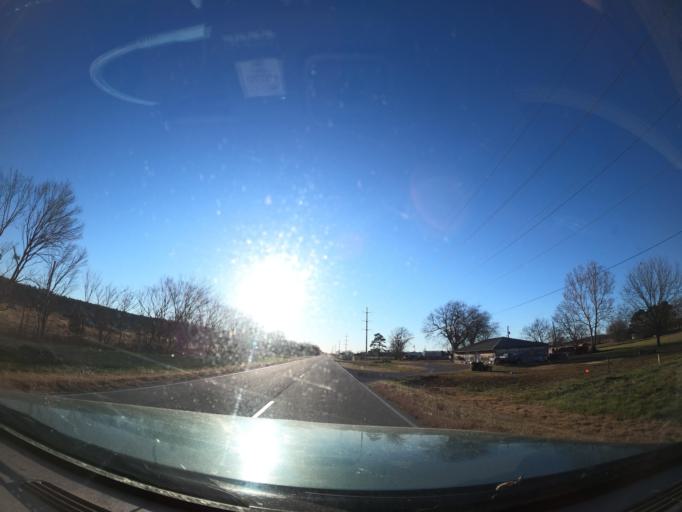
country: US
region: Oklahoma
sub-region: Pittsburg County
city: Hartshorne
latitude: 34.8822
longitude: -95.4952
